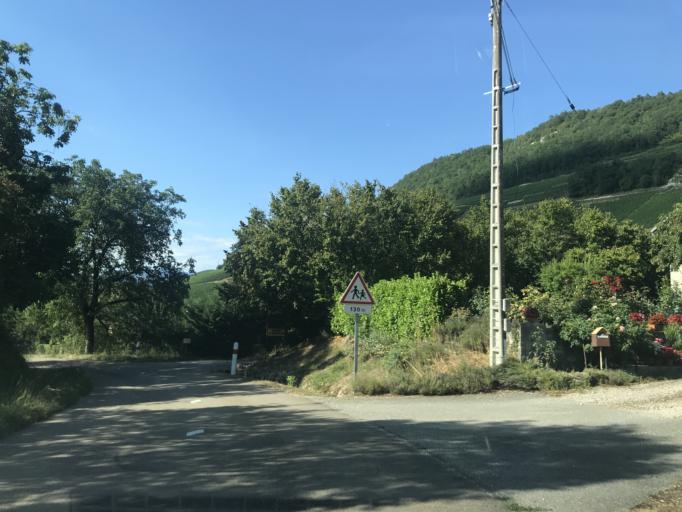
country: FR
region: Rhone-Alpes
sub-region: Departement de la Savoie
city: Yenne
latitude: 45.7390
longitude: 5.7984
